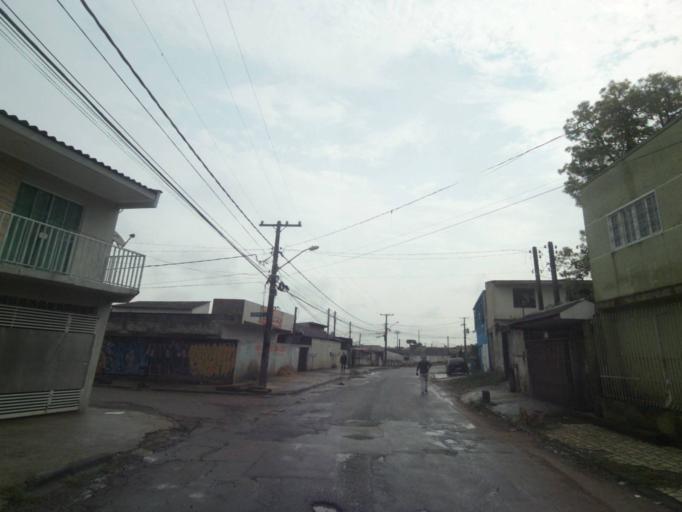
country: BR
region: Parana
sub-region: Curitiba
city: Curitiba
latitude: -25.4841
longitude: -49.3097
